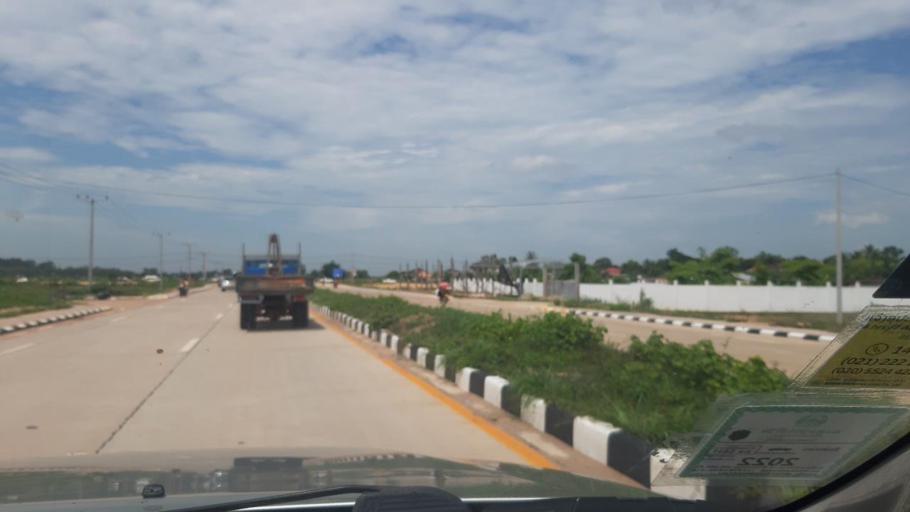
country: LA
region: Vientiane
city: Vientiane
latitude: 18.0335
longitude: 102.6107
